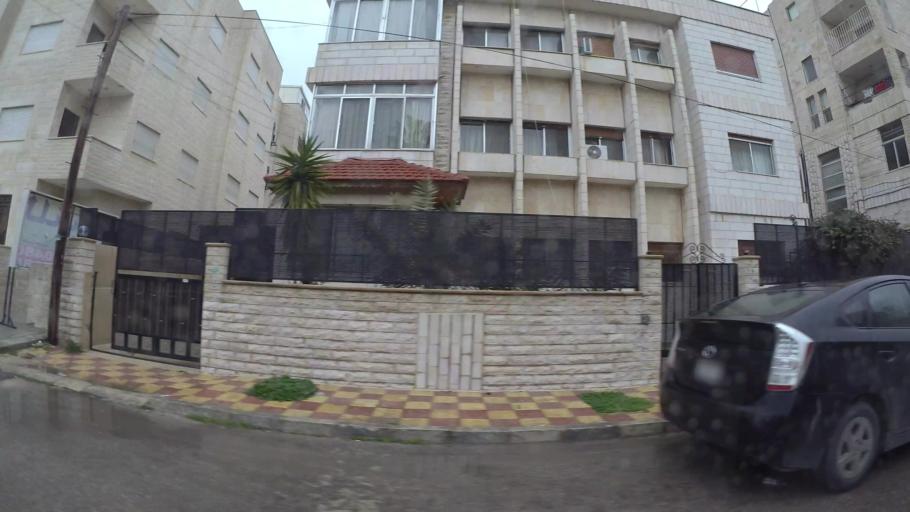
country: JO
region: Amman
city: Amman
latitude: 31.9725
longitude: 35.9161
